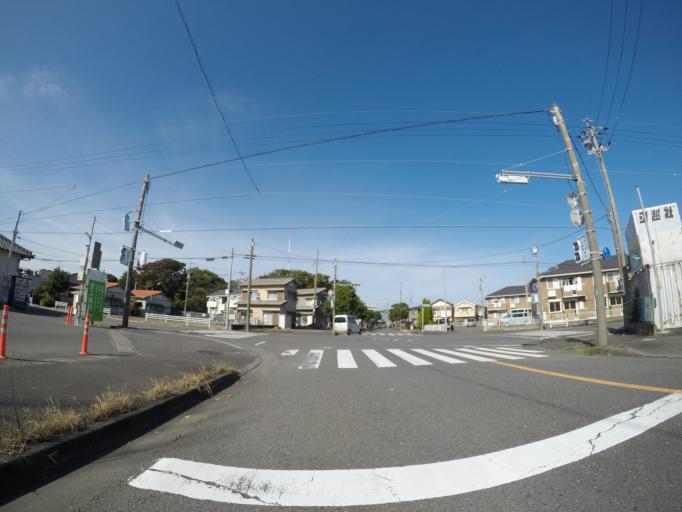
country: JP
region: Shizuoka
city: Shizuoka-shi
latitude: 34.9488
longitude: 138.4224
